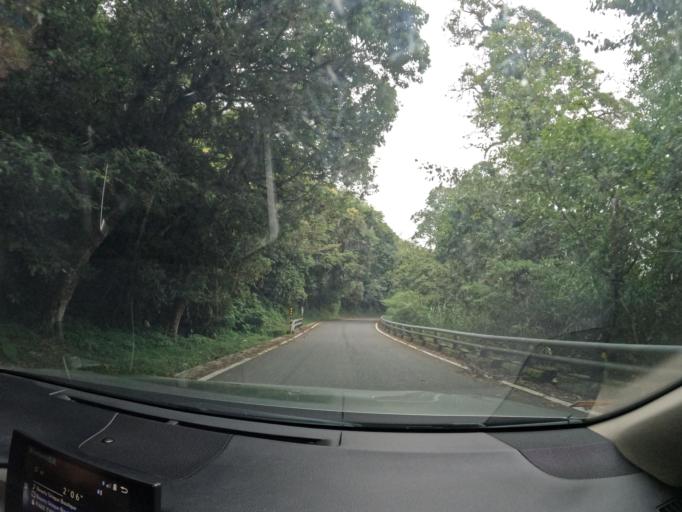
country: TW
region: Taiwan
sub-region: Taitung
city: Taitung
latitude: 23.2430
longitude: 120.9911
